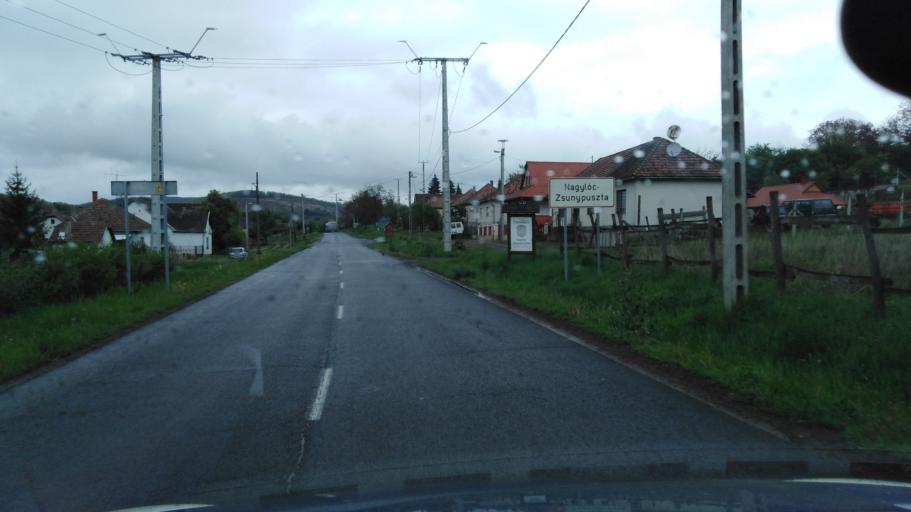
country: HU
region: Nograd
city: Rimoc
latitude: 47.9952
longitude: 19.6185
